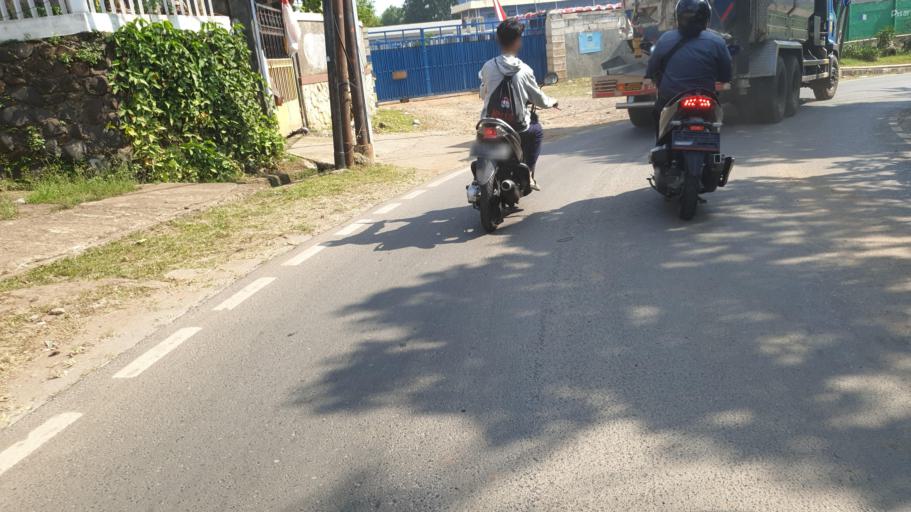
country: ID
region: Jakarta Raya
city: Jakarta
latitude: -6.2893
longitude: 106.8377
